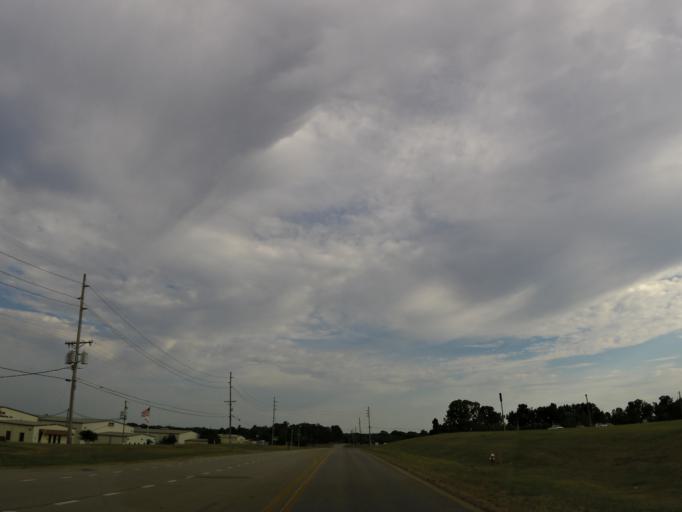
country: US
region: Alabama
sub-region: Morgan County
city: Trinity
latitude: 34.6290
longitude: -87.0385
